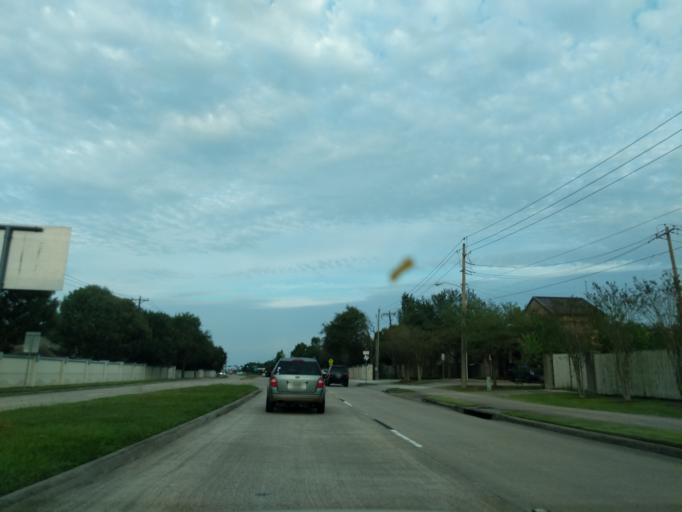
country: US
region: Texas
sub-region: Galveston County
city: Clear Lake Shores
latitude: 29.5264
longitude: -95.0468
